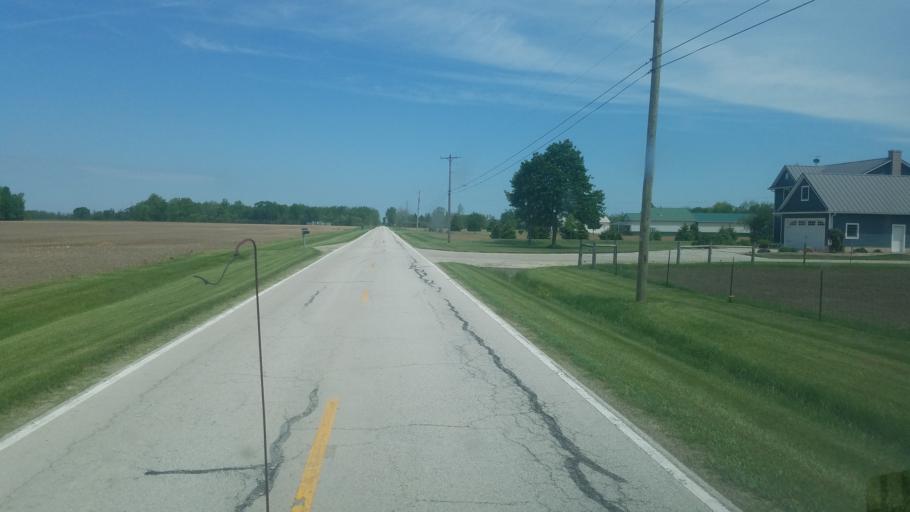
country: US
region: Ohio
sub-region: Sandusky County
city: Stony Prairie
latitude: 41.3947
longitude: -83.2027
